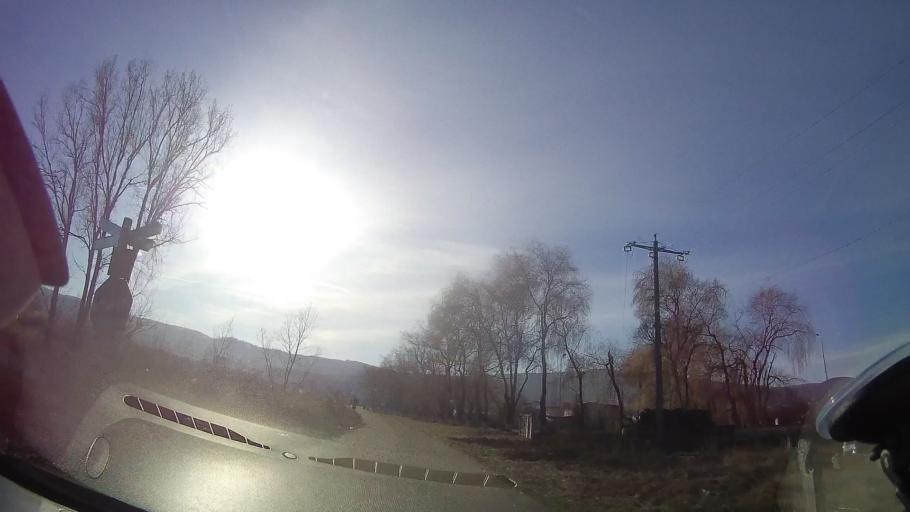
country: RO
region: Bihor
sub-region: Comuna Magesti
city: Magesti
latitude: 47.0130
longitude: 22.4566
